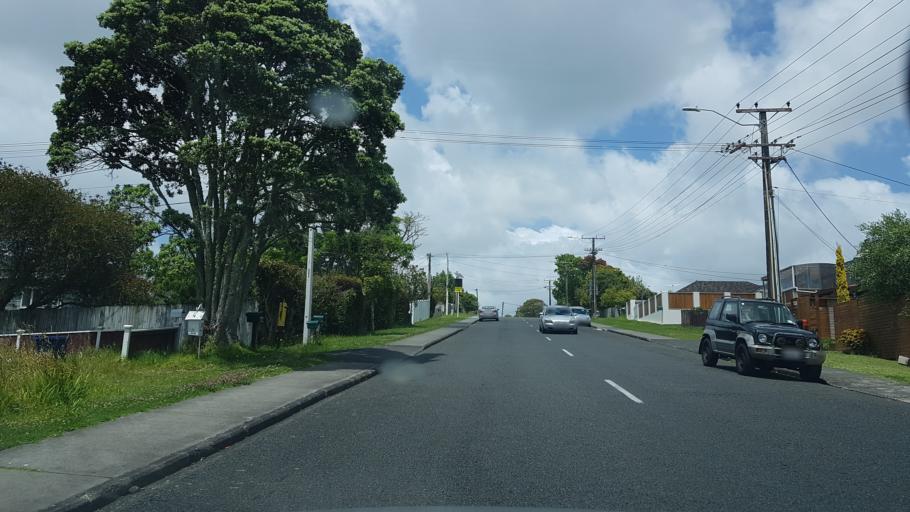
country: NZ
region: Auckland
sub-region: Auckland
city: North Shore
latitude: -36.7981
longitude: 174.7050
